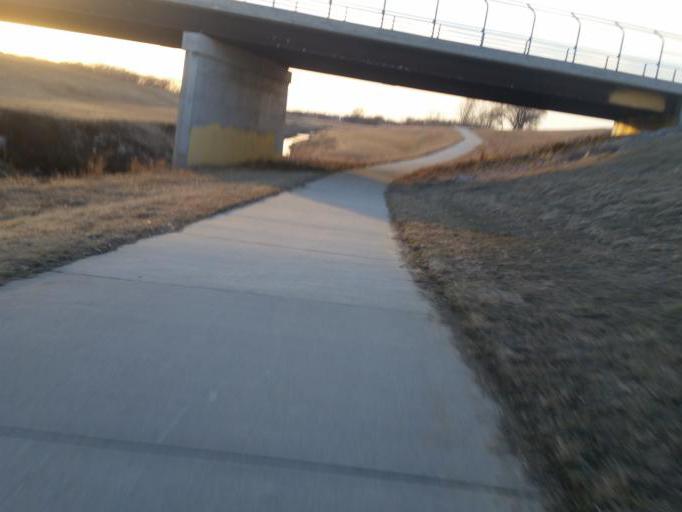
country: US
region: Nebraska
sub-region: Sarpy County
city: Papillion
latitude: 41.1495
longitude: -95.9855
